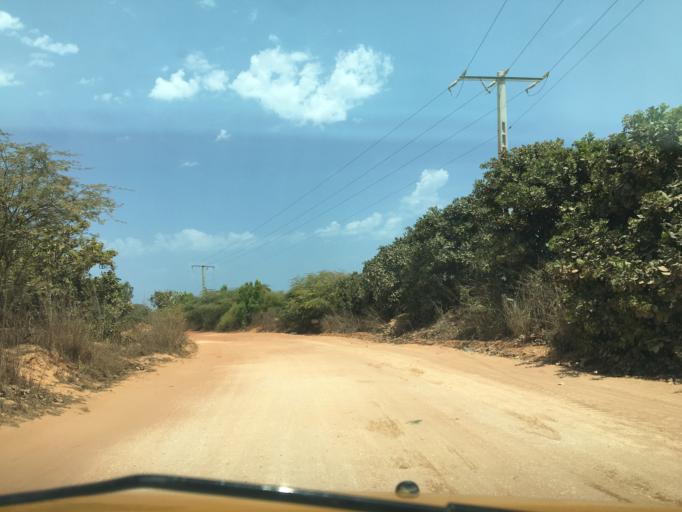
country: SN
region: Thies
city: Thies
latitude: 14.8172
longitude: -17.1970
